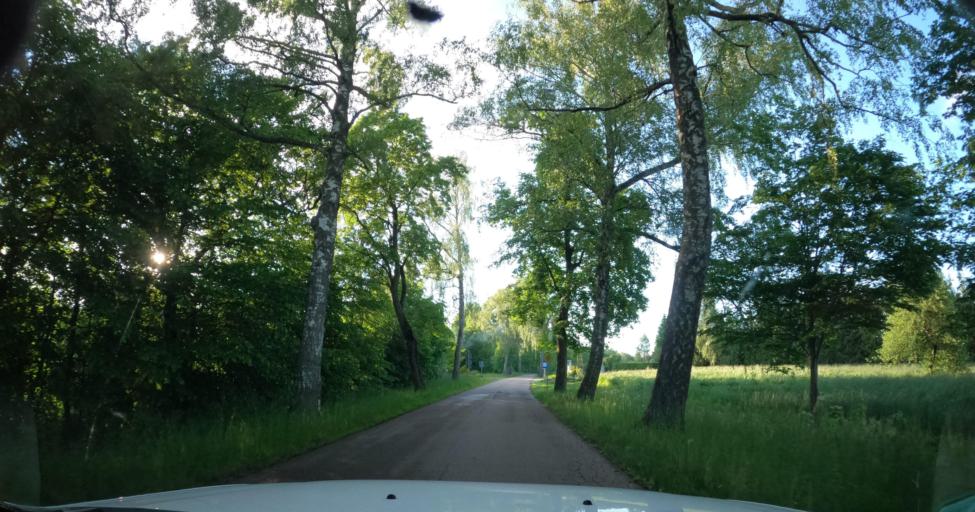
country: PL
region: Warmian-Masurian Voivodeship
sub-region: Powiat braniewski
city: Pieniezno
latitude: 54.2035
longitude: 20.0423
